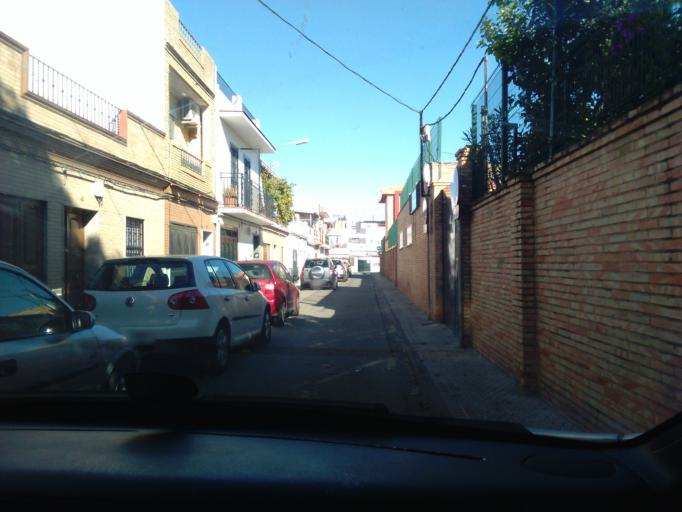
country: ES
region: Andalusia
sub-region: Provincia de Sevilla
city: Sevilla
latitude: 37.3847
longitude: -5.9066
